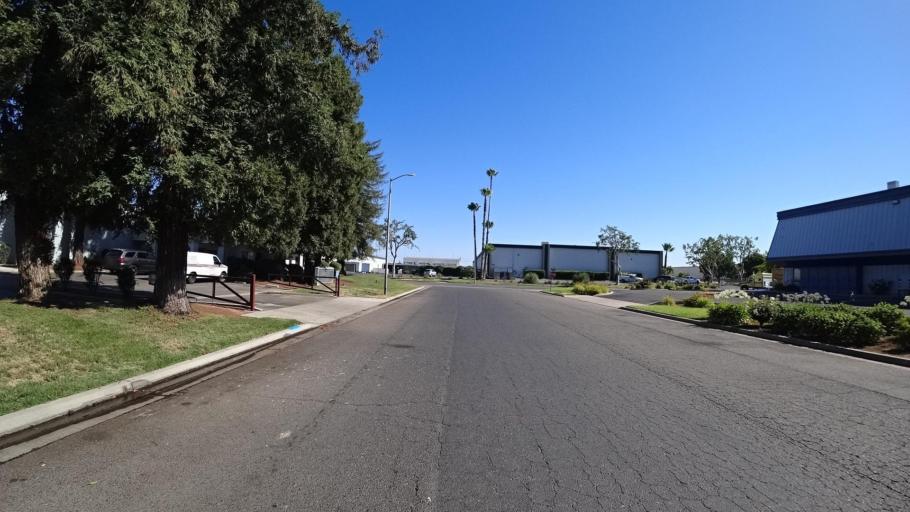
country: US
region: California
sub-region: Fresno County
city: Sunnyside
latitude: 36.7626
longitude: -119.7080
